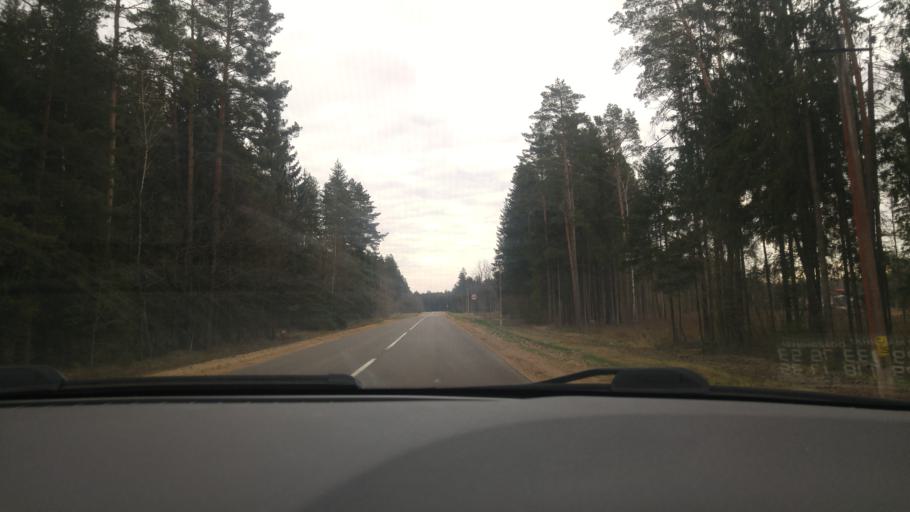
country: BY
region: Minsk
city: Chervyen'
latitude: 53.7337
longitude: 28.2942
